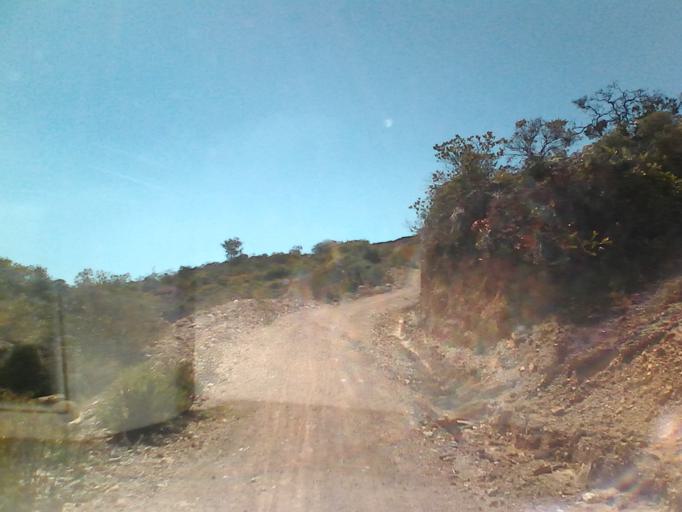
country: CO
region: Boyaca
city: Sachica
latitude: 5.5369
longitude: -73.5513
